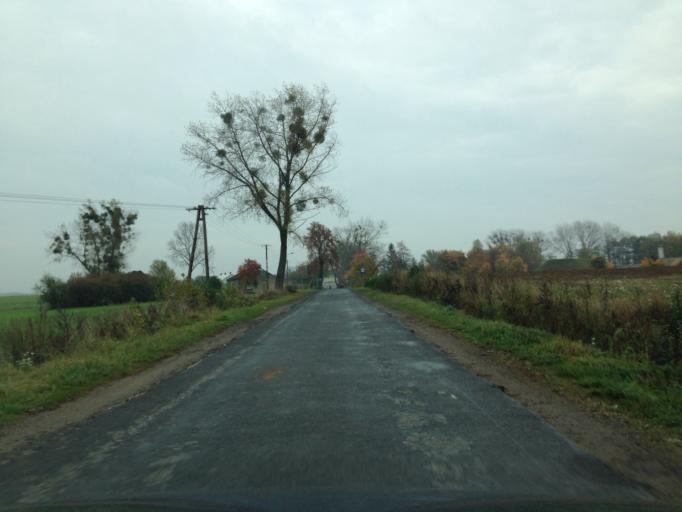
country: PL
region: Kujawsko-Pomorskie
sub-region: Powiat brodnicki
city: Swiedziebnia
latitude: 53.1568
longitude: 19.5146
